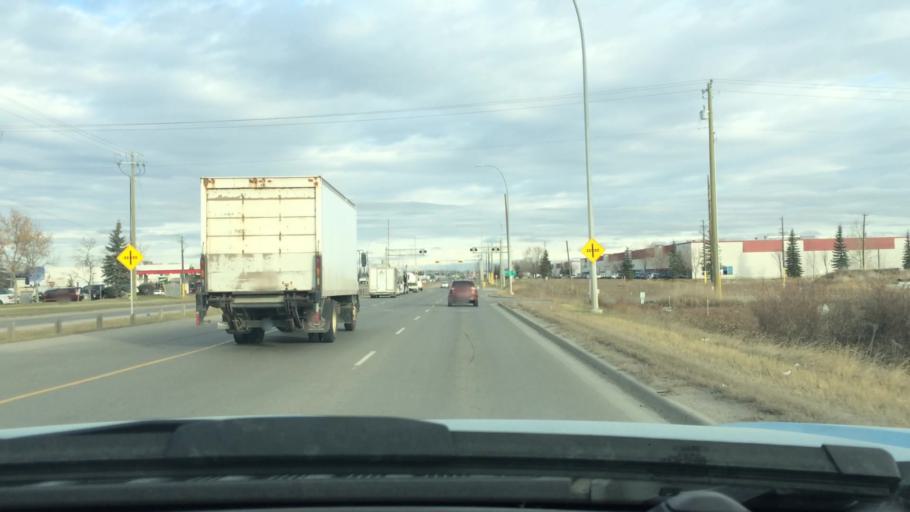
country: CA
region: Alberta
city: Calgary
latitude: 51.0072
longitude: -113.9583
